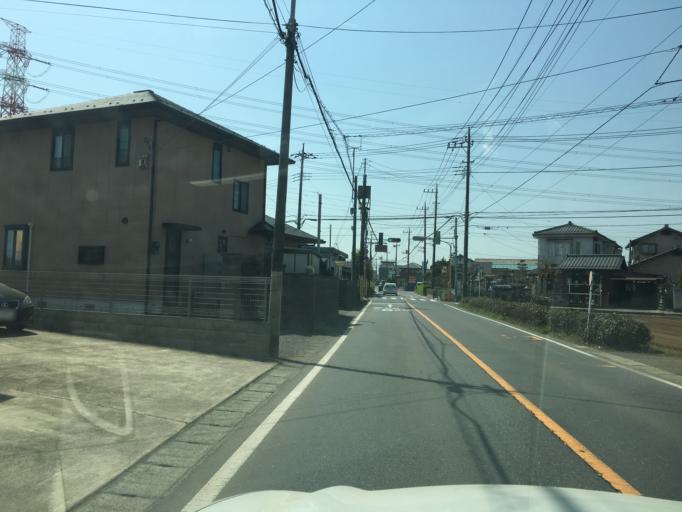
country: JP
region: Saitama
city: Sayama
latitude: 35.8427
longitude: 139.4437
